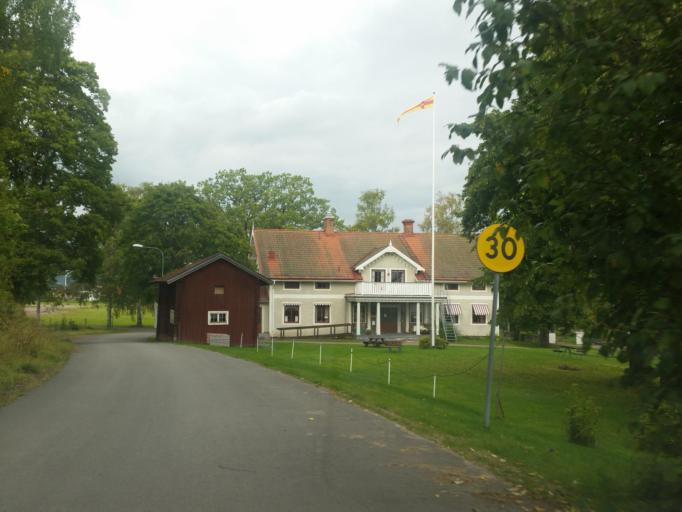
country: SE
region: Dalarna
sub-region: Leksand Municipality
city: Smedby
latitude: 60.6814
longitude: 15.1017
